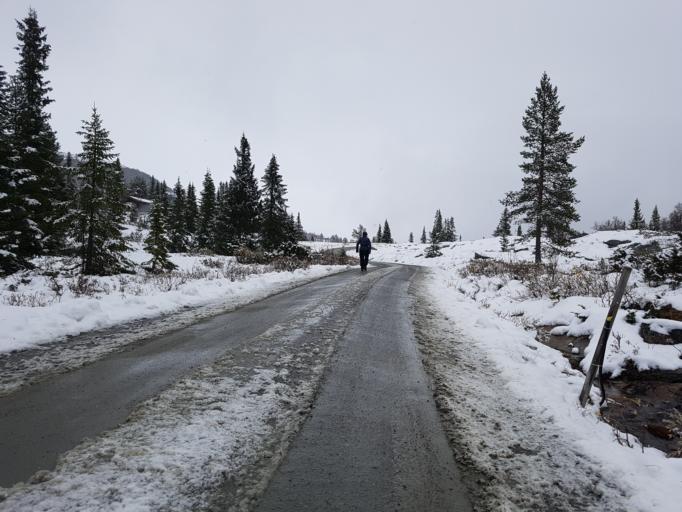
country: NO
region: Oppland
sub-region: Sel
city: Otta
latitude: 61.8059
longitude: 9.6894
